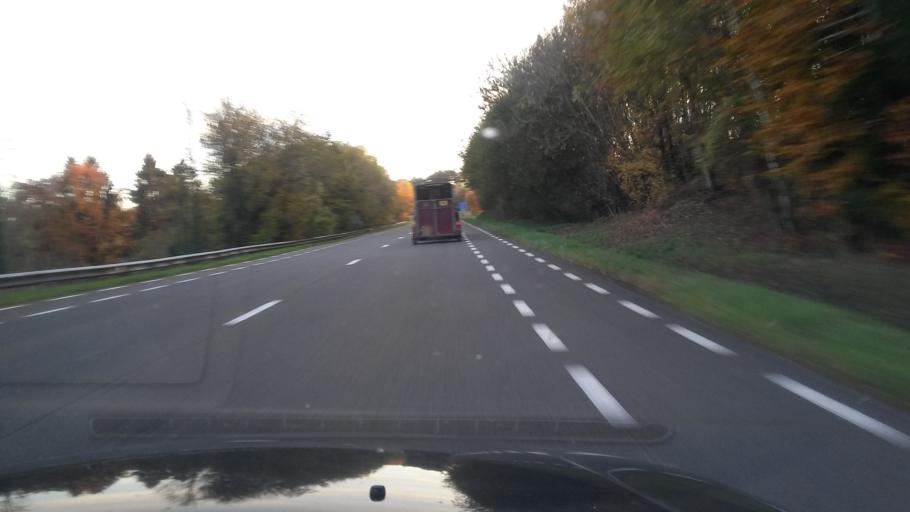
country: BE
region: Wallonia
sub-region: Province du Luxembourg
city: Florenville
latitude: 49.7052
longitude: 5.2591
